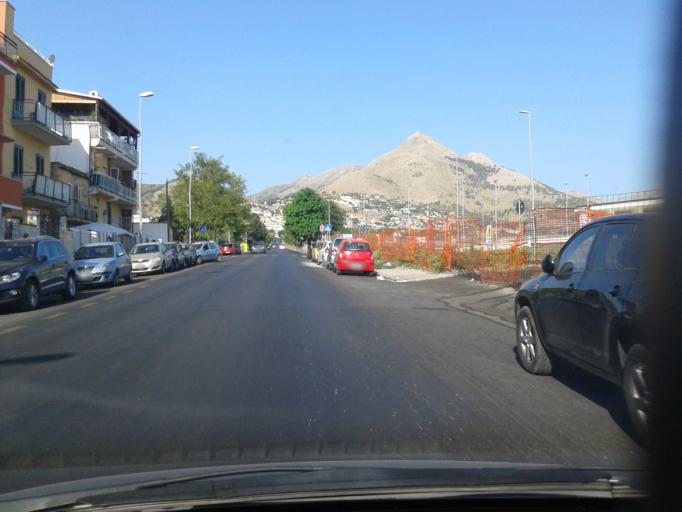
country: IT
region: Sicily
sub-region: Palermo
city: Palermo
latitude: 38.1102
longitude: 13.3197
